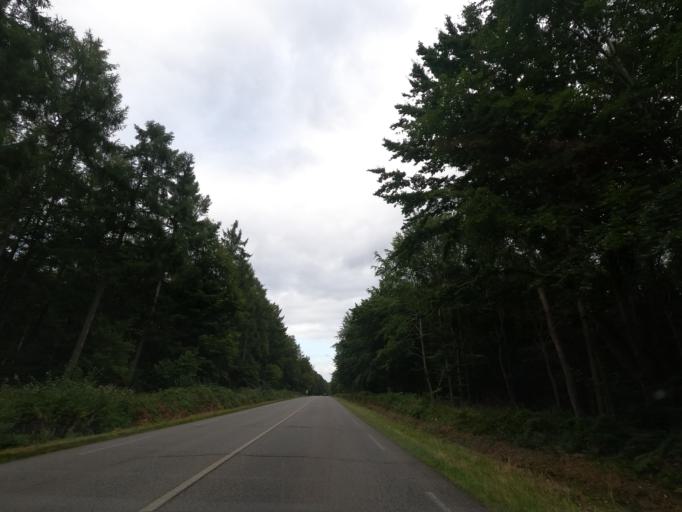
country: FR
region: Haute-Normandie
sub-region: Departement de l'Eure
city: Bourgtheroulde-Infreville
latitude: 49.3254
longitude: 0.9079
